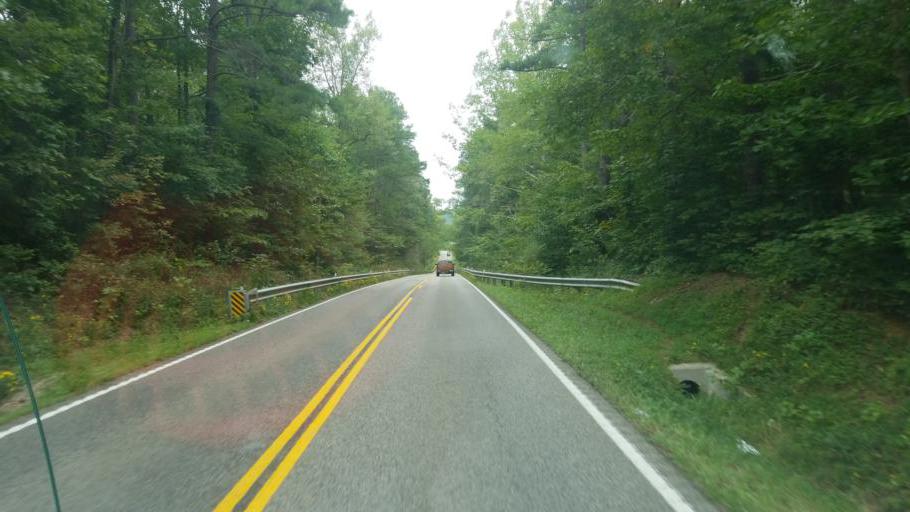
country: US
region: Kentucky
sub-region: Rowan County
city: Morehead
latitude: 38.2245
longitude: -83.4668
